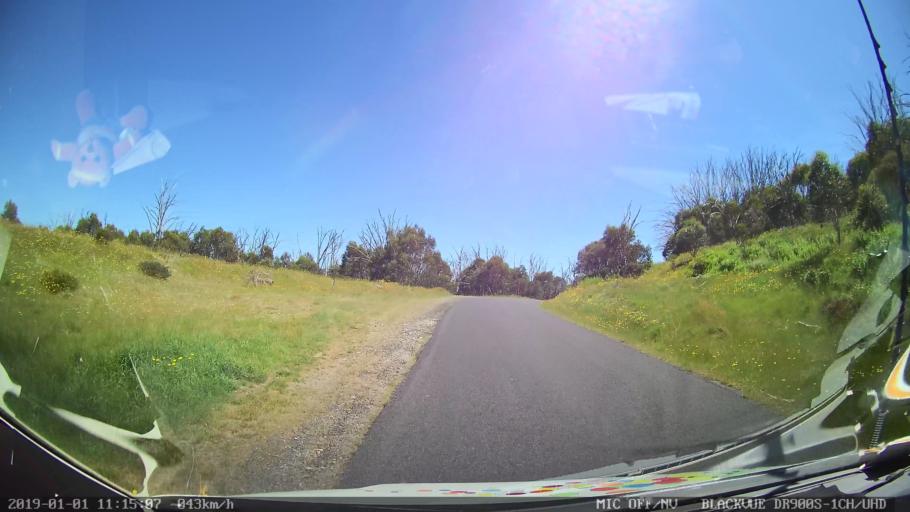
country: AU
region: New South Wales
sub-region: Snowy River
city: Jindabyne
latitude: -35.9470
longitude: 148.3866
